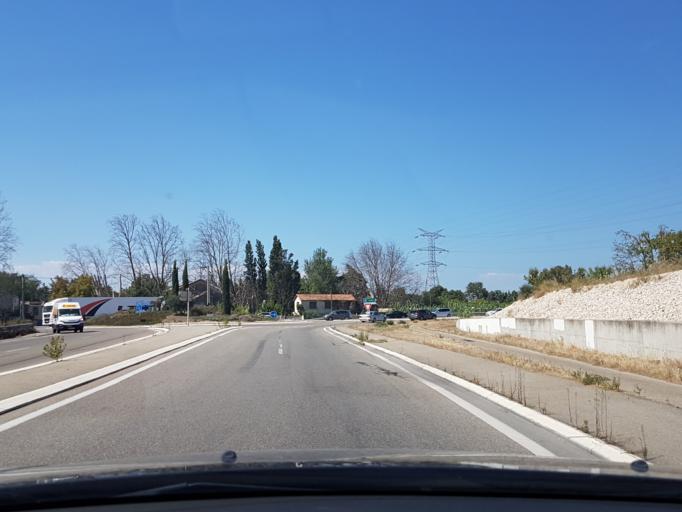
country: FR
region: Provence-Alpes-Cote d'Azur
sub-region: Departement des Bouches-du-Rhone
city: Rognonas
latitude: 43.9111
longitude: 4.8079
